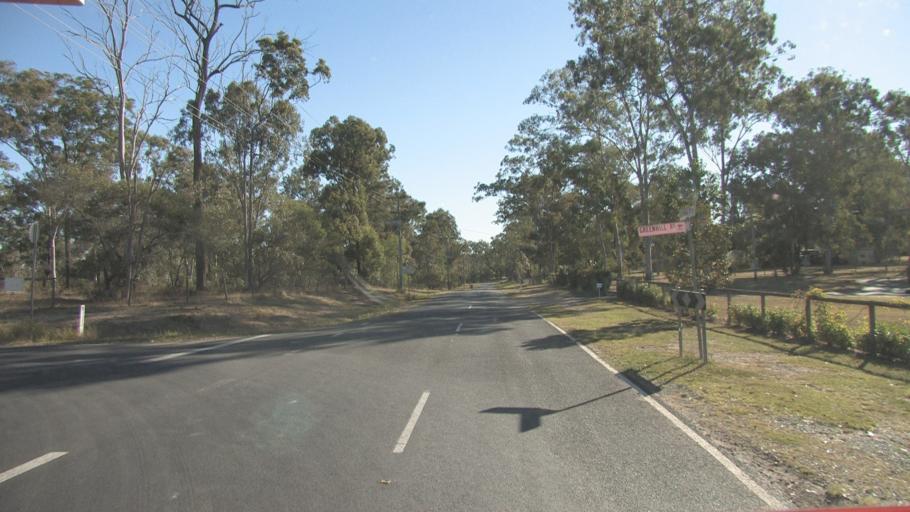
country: AU
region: Queensland
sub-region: Logan
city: Park Ridge South
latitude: -27.7357
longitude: 153.0180
